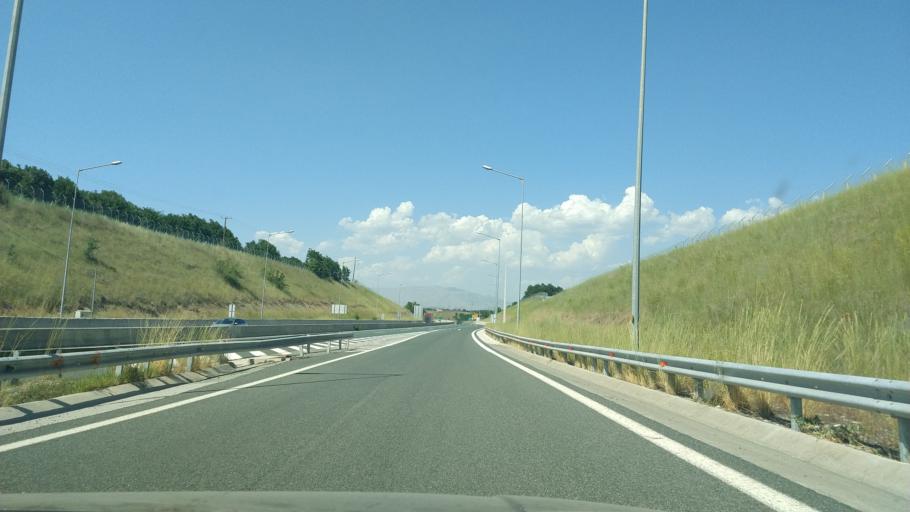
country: GR
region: West Macedonia
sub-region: Nomos Grevenon
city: Grevena
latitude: 40.0675
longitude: 21.4402
